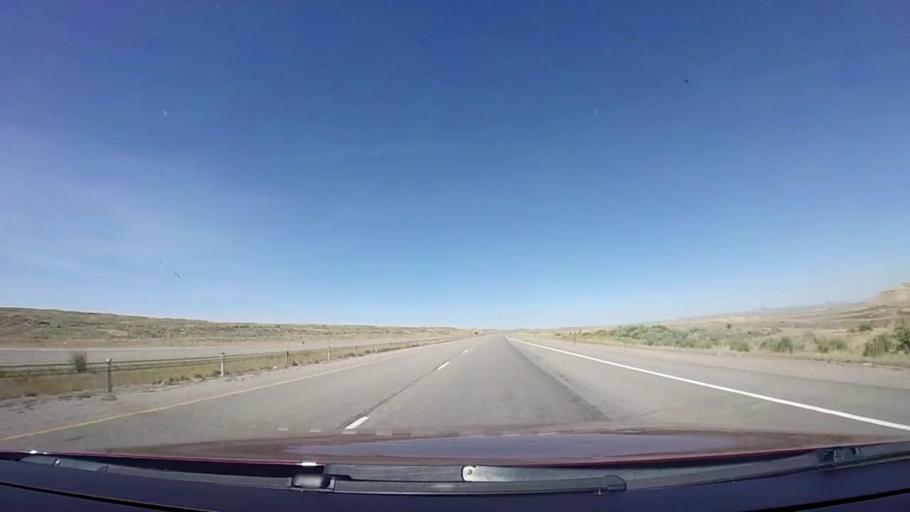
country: US
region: Wyoming
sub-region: Sweetwater County
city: Rock Springs
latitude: 41.6480
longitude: -108.6905
